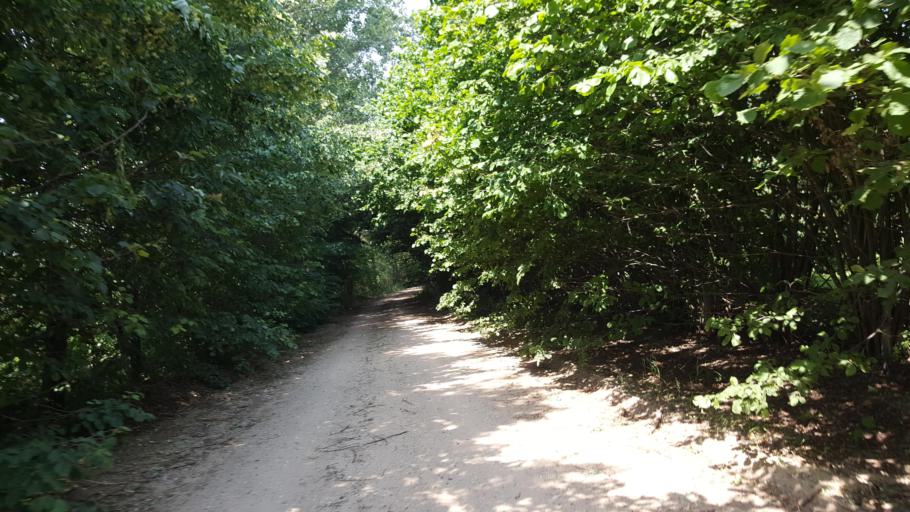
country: BY
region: Brest
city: Kamyanyets
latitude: 52.3620
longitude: 23.7622
